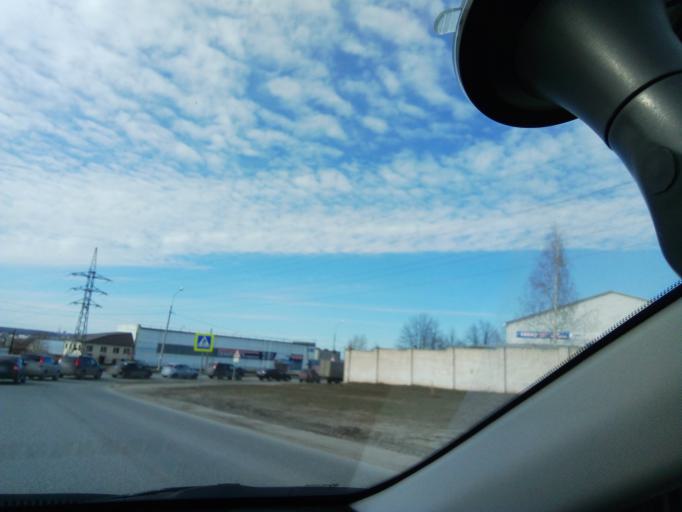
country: RU
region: Chuvashia
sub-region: Cheboksarskiy Rayon
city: Cheboksary
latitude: 56.1001
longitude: 47.2529
